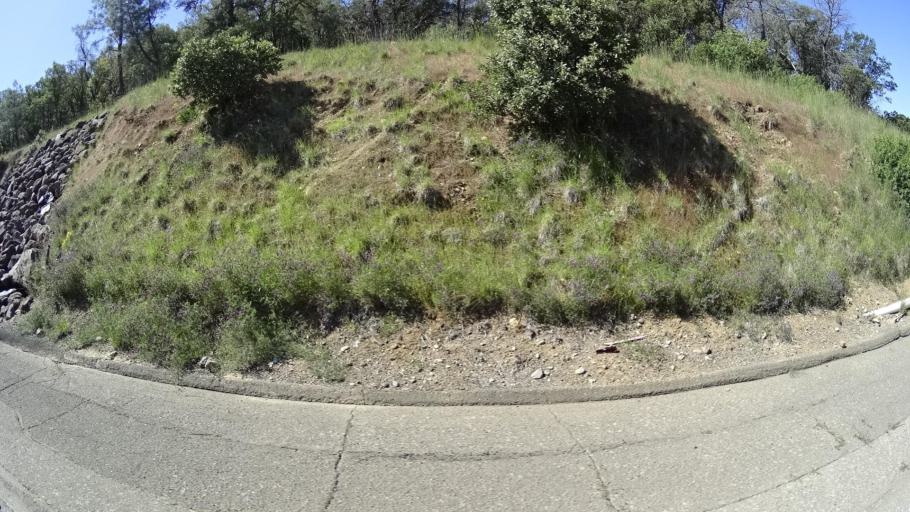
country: US
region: California
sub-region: Lake County
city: Hidden Valley Lake
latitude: 38.8928
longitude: -122.4843
